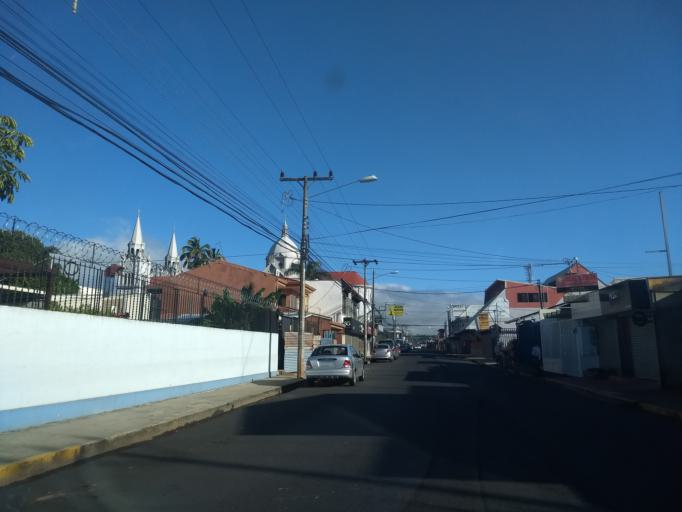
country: CR
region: Alajuela
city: San Ramon
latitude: 10.0858
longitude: -84.4690
